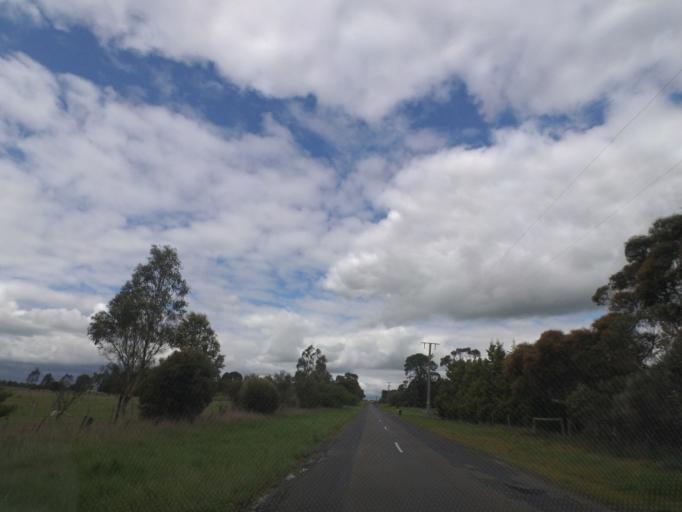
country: AU
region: Victoria
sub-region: Hume
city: Craigieburn
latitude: -37.4660
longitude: 144.9441
